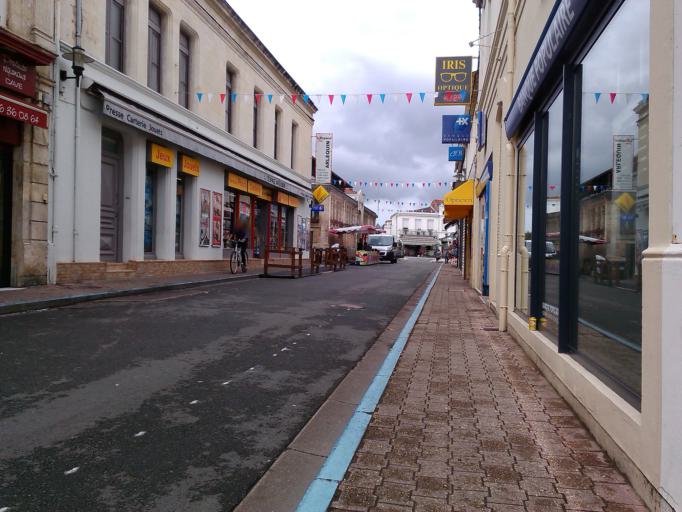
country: FR
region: Poitou-Charentes
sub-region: Departement de la Charente-Maritime
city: La Tremblade
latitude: 45.7688
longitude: -1.1405
